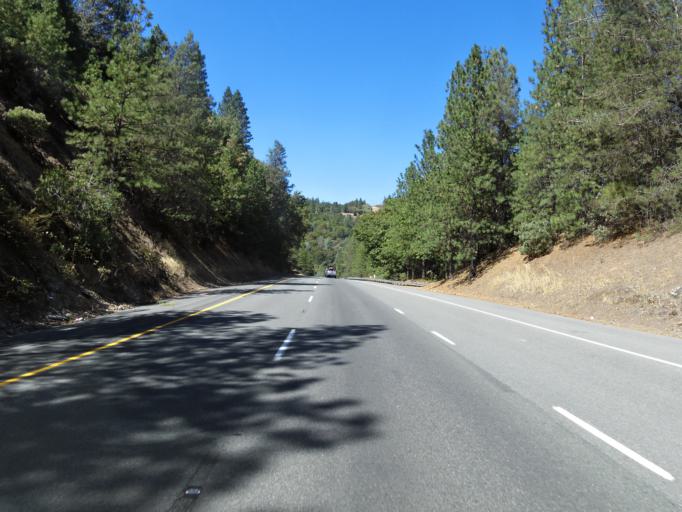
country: US
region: California
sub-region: Shasta County
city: Shasta Lake
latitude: 40.7742
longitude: -122.3126
